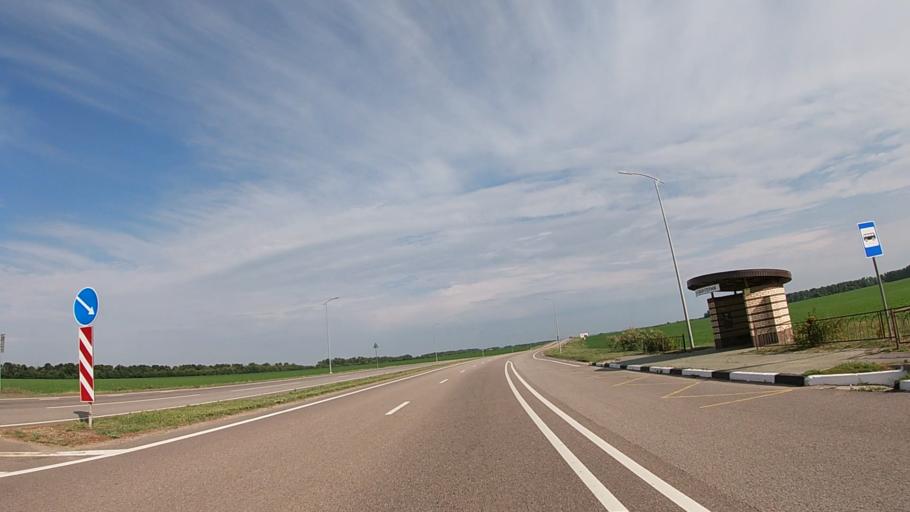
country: RU
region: Belgorod
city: Rakitnoye
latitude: 50.7922
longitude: 35.8660
